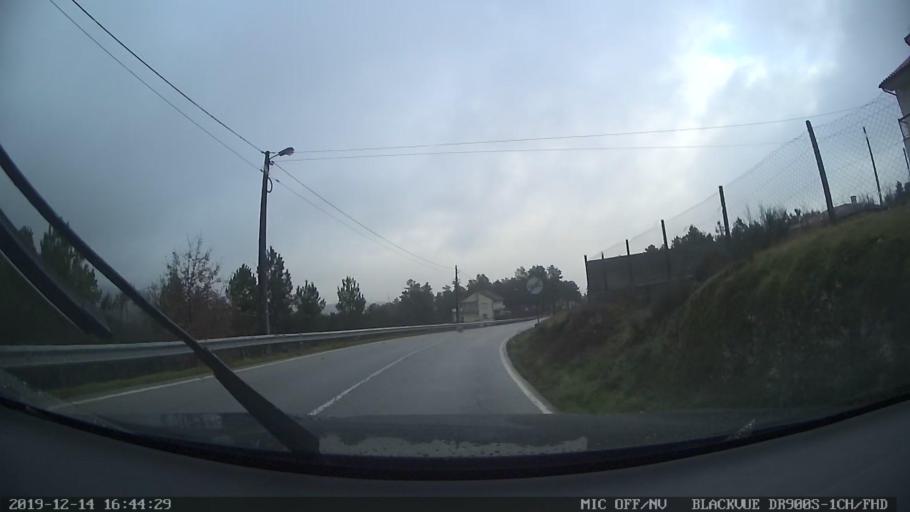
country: PT
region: Vila Real
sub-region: Murca
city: Murca
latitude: 41.3919
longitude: -7.4950
